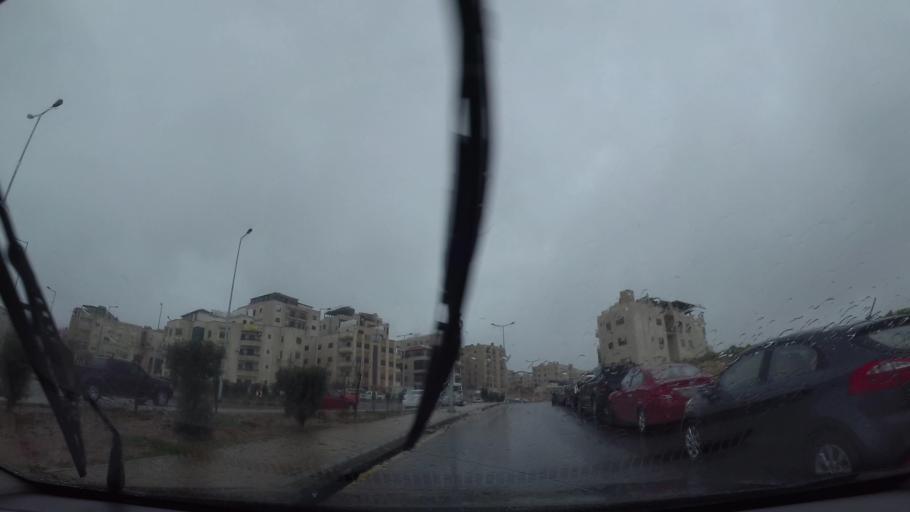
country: JO
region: Amman
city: Al Jubayhah
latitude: 32.0165
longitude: 35.8902
